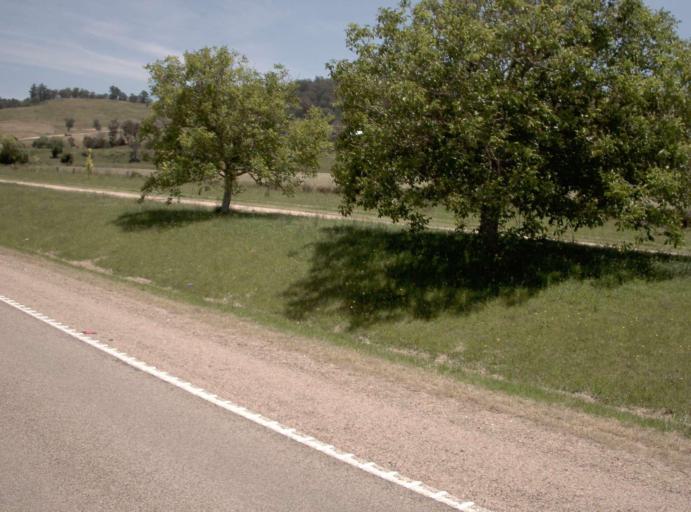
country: AU
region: Victoria
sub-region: East Gippsland
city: Lakes Entrance
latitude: -37.7094
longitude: 147.8211
